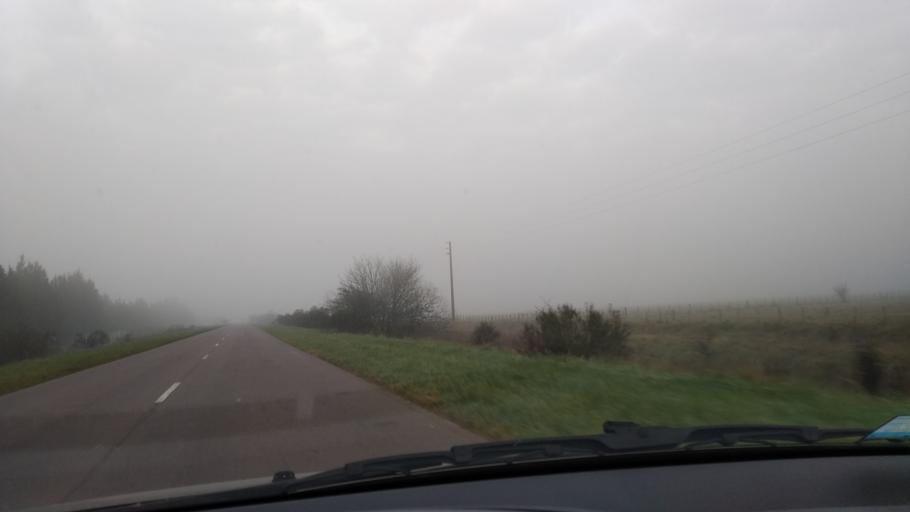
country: AR
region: Buenos Aires
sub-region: Partido de San Vicente
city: San Vicente
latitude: -35.2489
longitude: -58.4918
